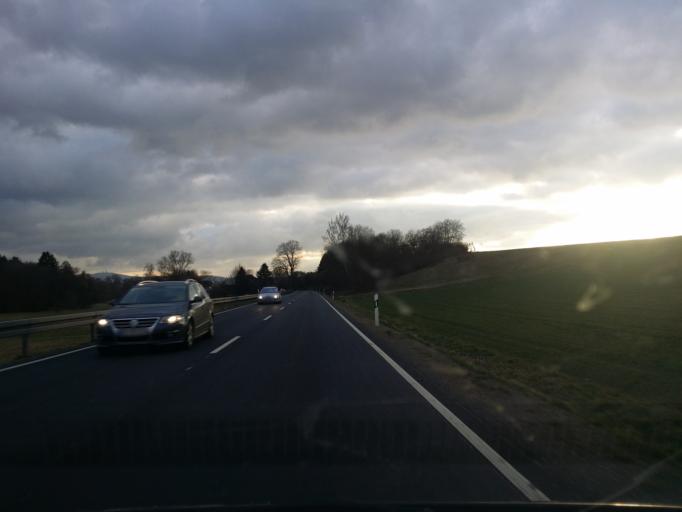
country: DE
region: Hesse
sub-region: Regierungsbezirk Darmstadt
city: Usingen
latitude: 50.3379
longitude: 8.5581
